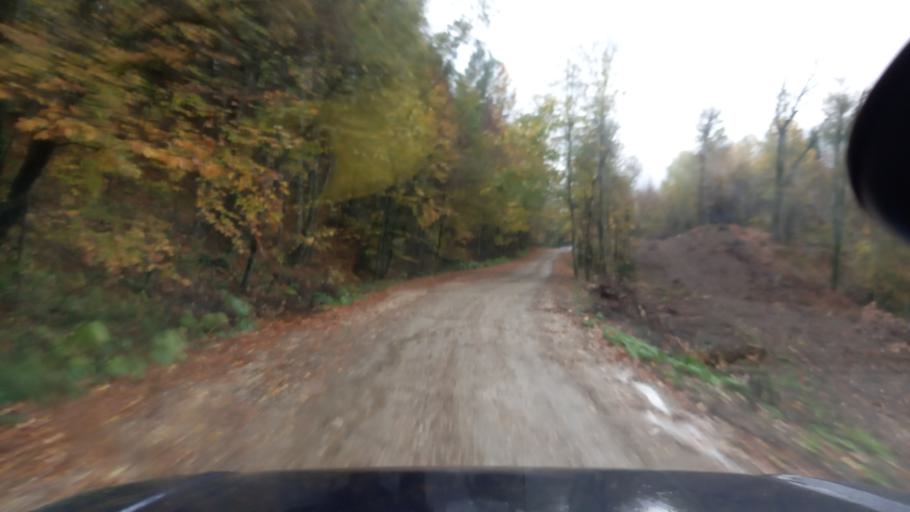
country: RU
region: Krasnodarskiy
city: Neftegorsk
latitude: 44.0424
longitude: 39.8334
